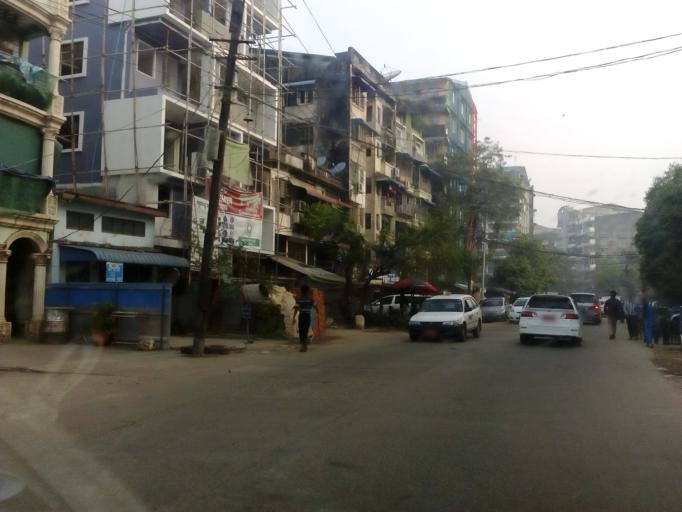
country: MM
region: Yangon
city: Yangon
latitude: 16.8068
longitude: 96.1793
